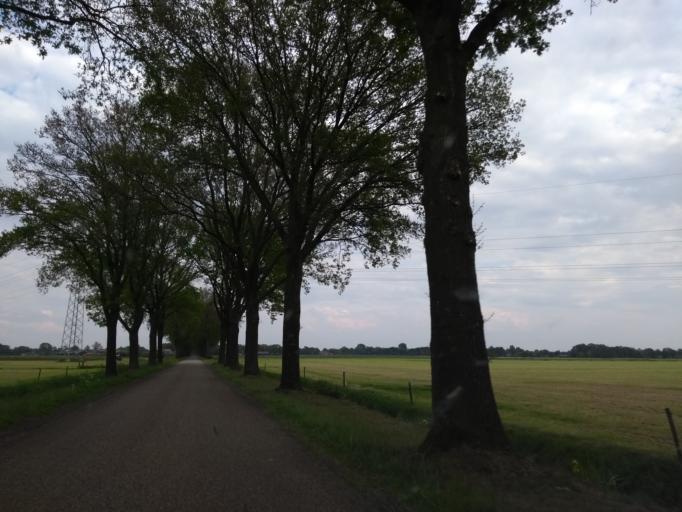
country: NL
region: Overijssel
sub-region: Gemeente Almelo
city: Almelo
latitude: 52.3946
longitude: 6.6783
